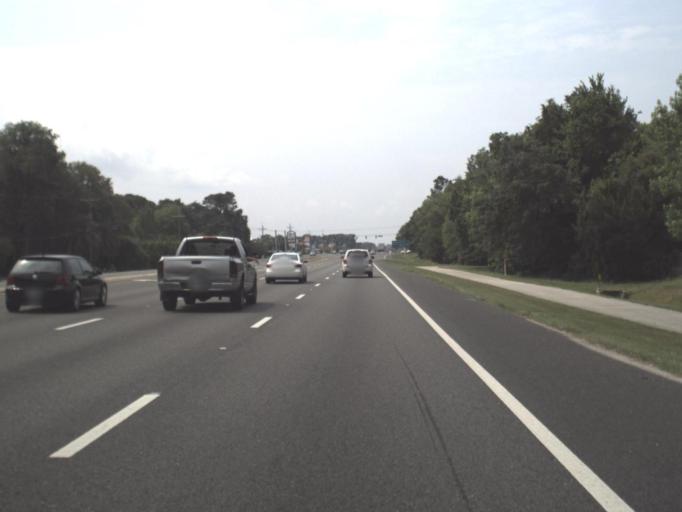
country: US
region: Florida
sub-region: Clay County
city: Orange Park
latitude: 30.1409
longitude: -81.7016
